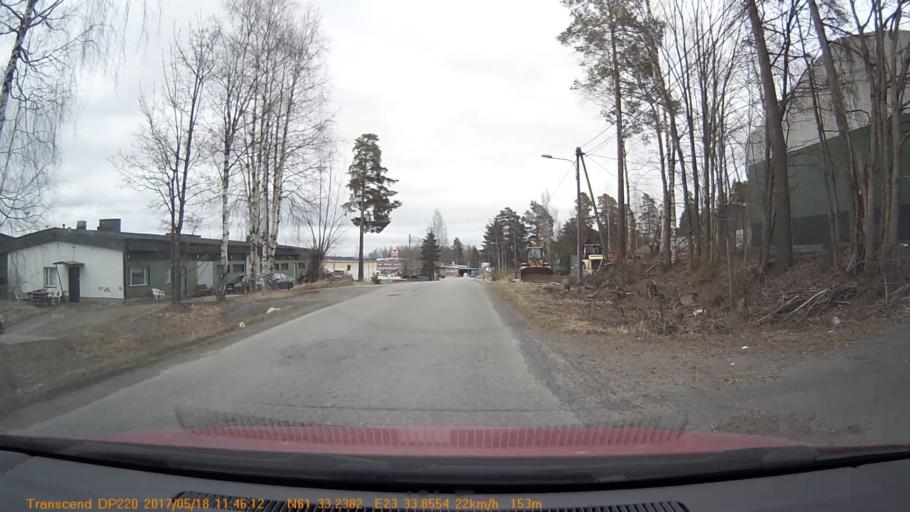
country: FI
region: Pirkanmaa
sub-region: Tampere
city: Yloejaervi
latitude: 61.5540
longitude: 23.5643
